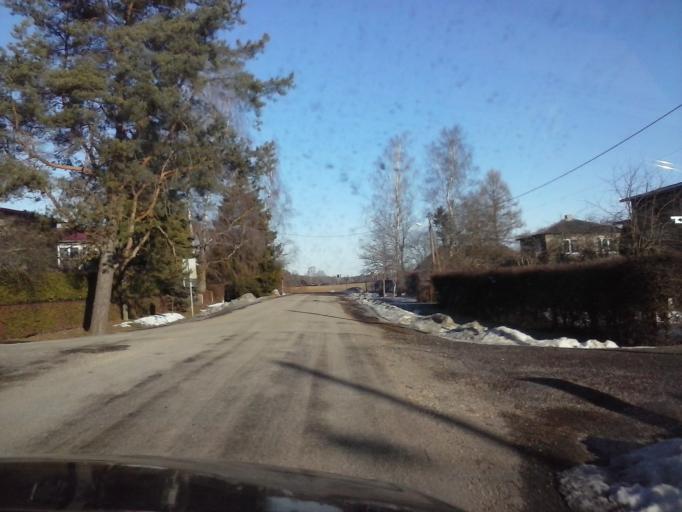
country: EE
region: Tartu
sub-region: Elva linn
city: Elva
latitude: 58.0463
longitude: 26.4739
